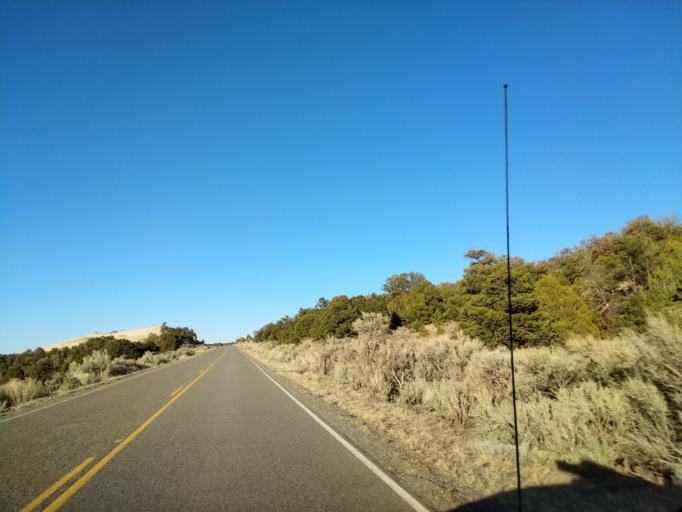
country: US
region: Colorado
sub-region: Mesa County
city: Redlands
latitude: 38.9844
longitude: -108.7920
